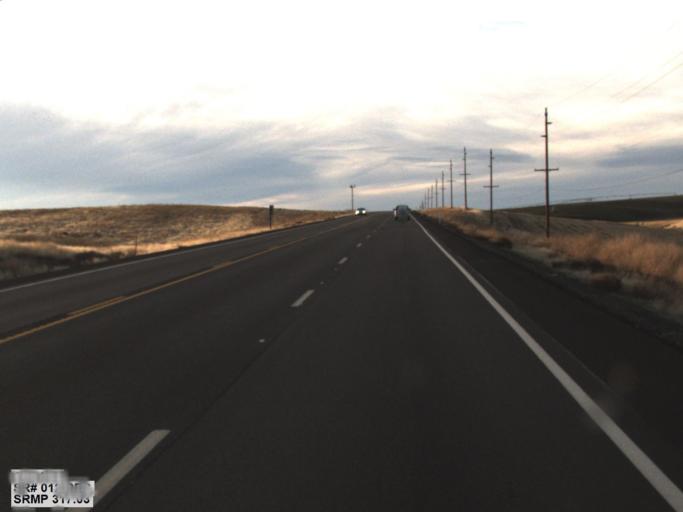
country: US
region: Washington
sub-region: Walla Walla County
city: Burbank
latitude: 46.0575
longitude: -118.7262
